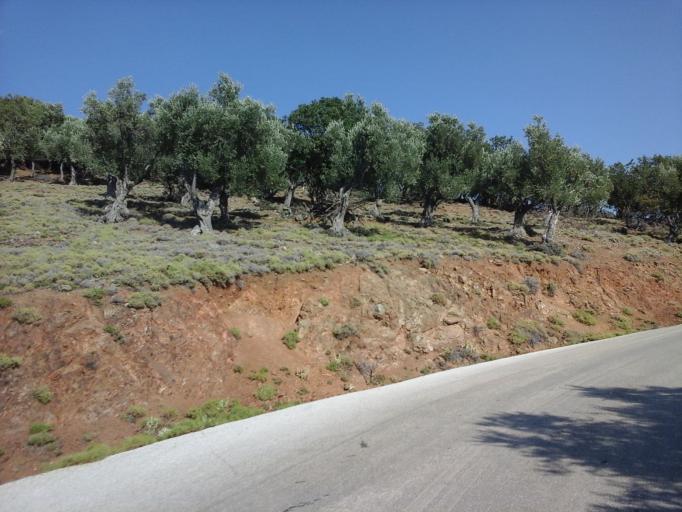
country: GR
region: East Macedonia and Thrace
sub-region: Nomos Evrou
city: Samothraki
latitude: 40.4185
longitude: 25.5458
